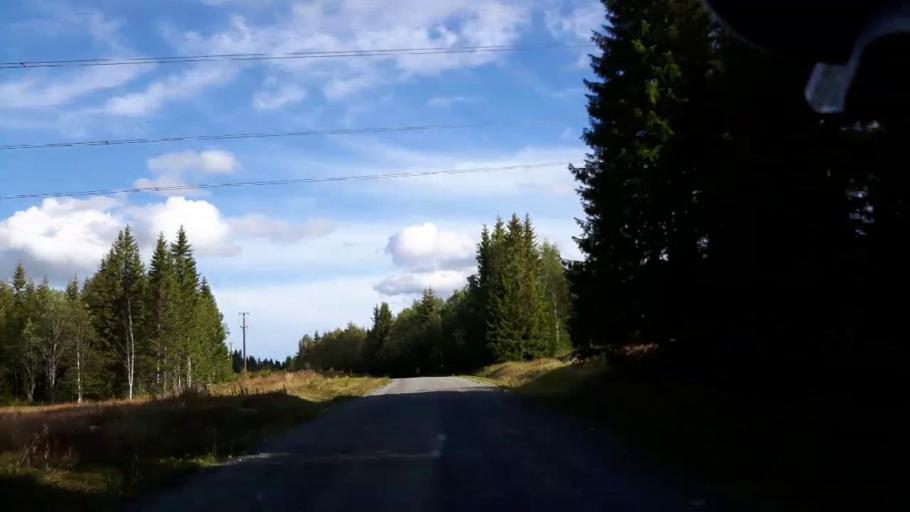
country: SE
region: Jaemtland
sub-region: Ragunda Kommun
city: Hammarstrand
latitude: 63.4425
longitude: 15.9783
